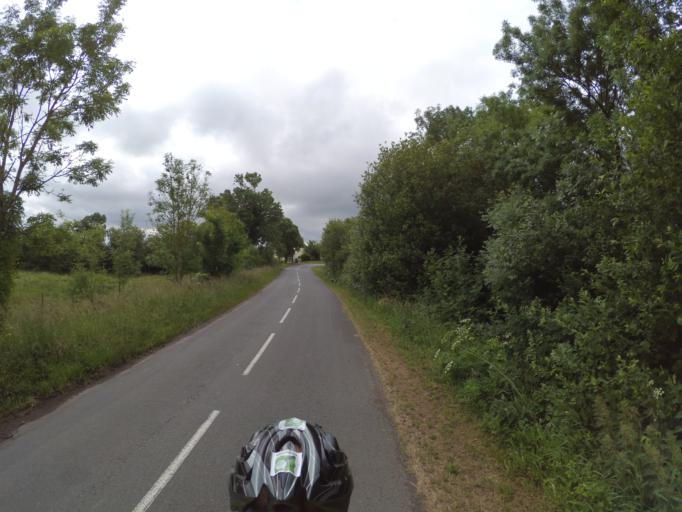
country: FR
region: Poitou-Charentes
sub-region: Departement de la Charente-Maritime
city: Yves
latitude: 46.0215
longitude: -1.0460
